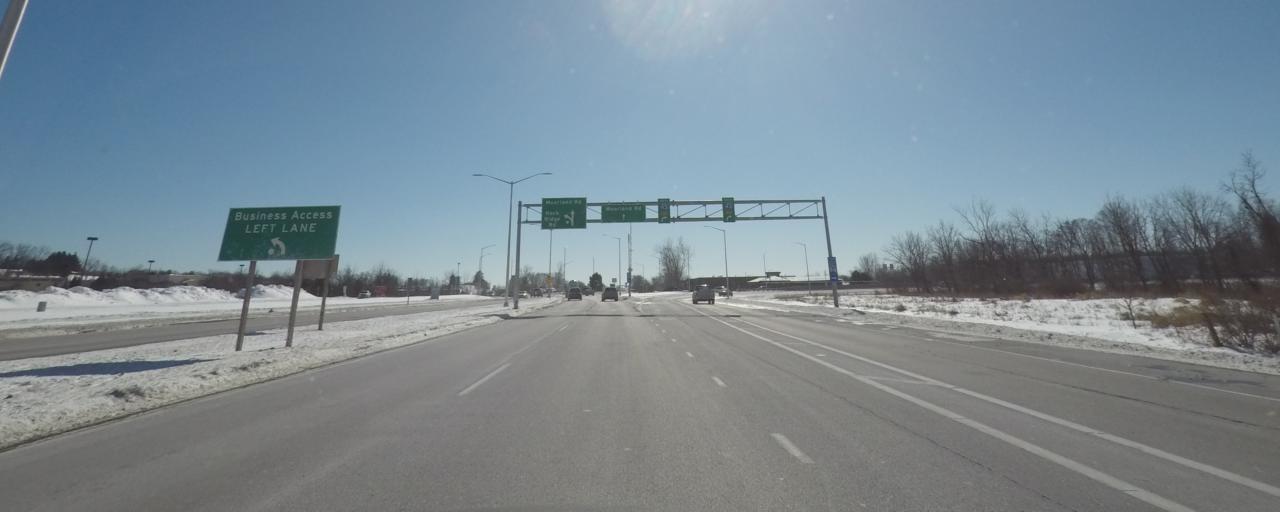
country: US
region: Wisconsin
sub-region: Waukesha County
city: New Berlin
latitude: 42.9510
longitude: -88.1091
